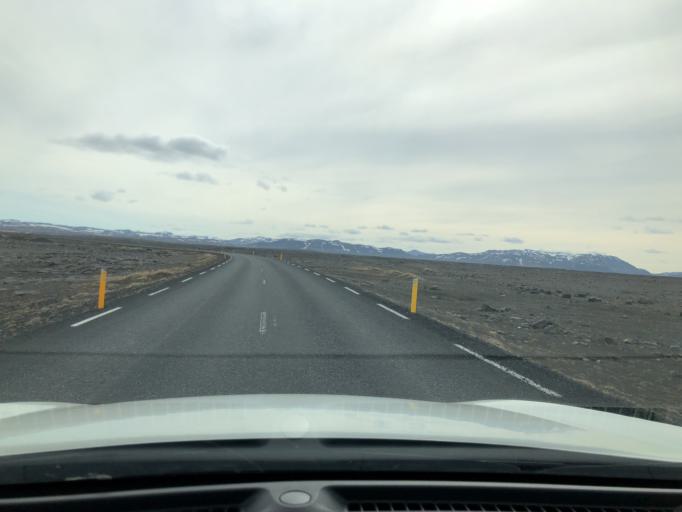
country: IS
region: Northeast
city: Laugar
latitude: 65.6200
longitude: -16.2319
